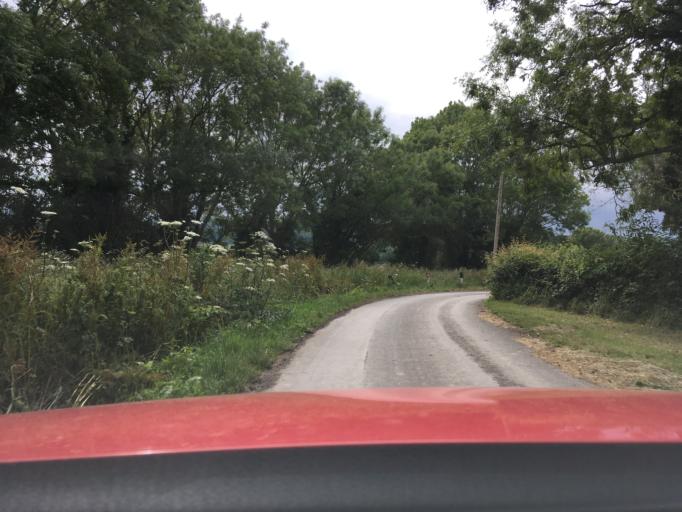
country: GB
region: England
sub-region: Gloucestershire
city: Cinderford
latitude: 51.7989
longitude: -2.4402
